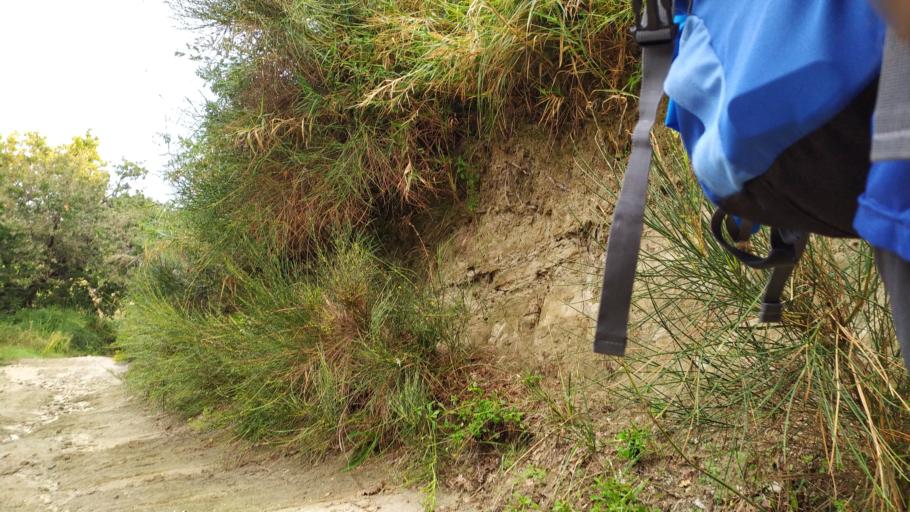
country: IT
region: Sicily
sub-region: Messina
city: Villafranca Tirrena
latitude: 38.2153
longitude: 15.4740
